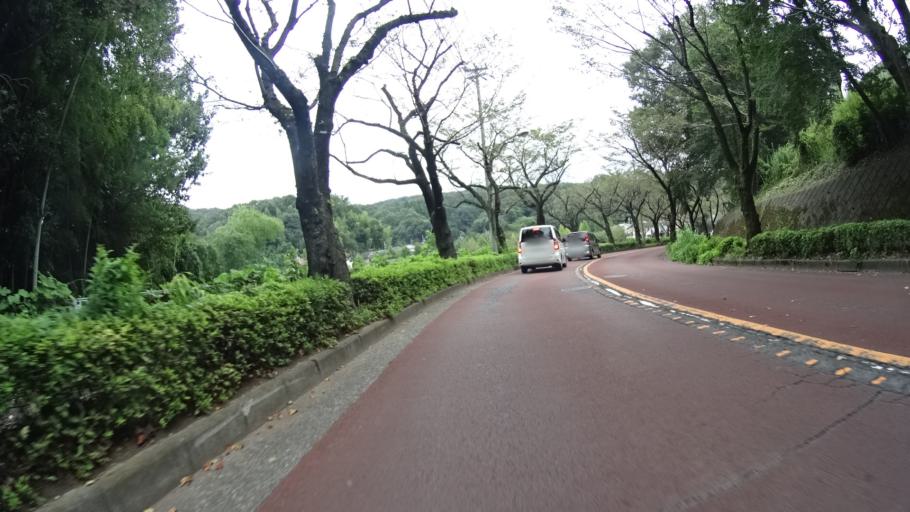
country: JP
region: Tokyo
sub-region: Machida-shi
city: Machida
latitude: 35.5939
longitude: 139.4224
